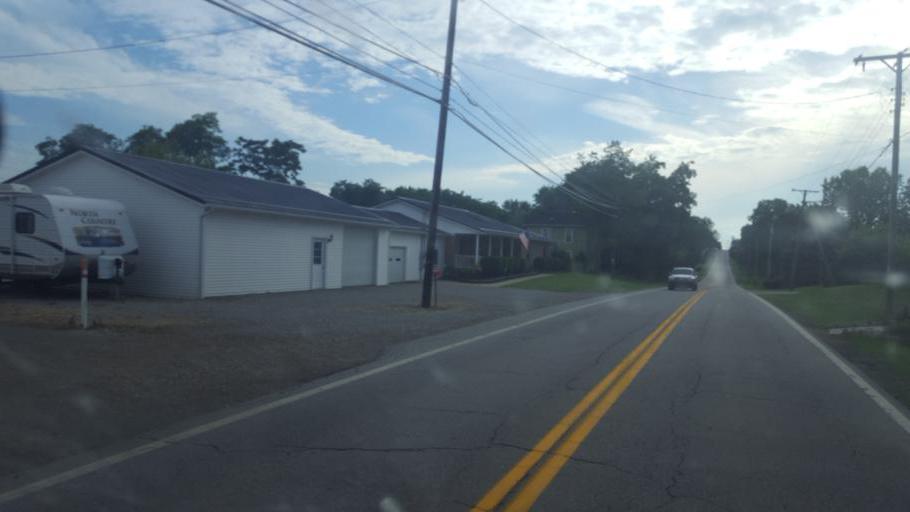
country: US
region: Ohio
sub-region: Ashland County
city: Ashland
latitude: 40.7734
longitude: -82.2554
